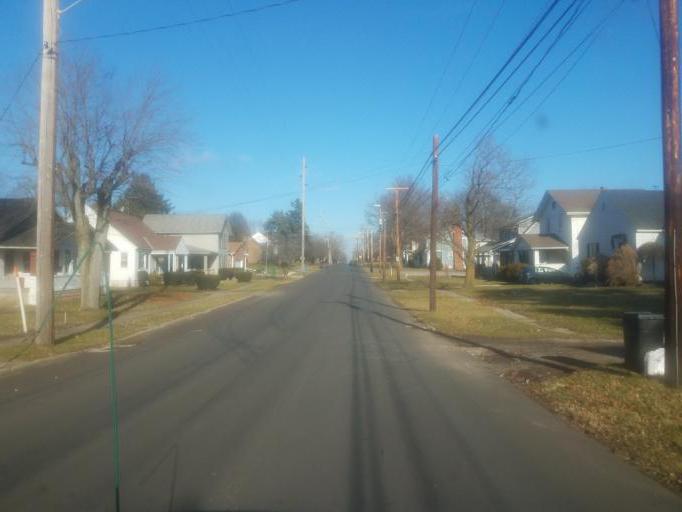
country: US
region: Ohio
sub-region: Crawford County
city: Galion
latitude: 40.7395
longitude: -82.7835
